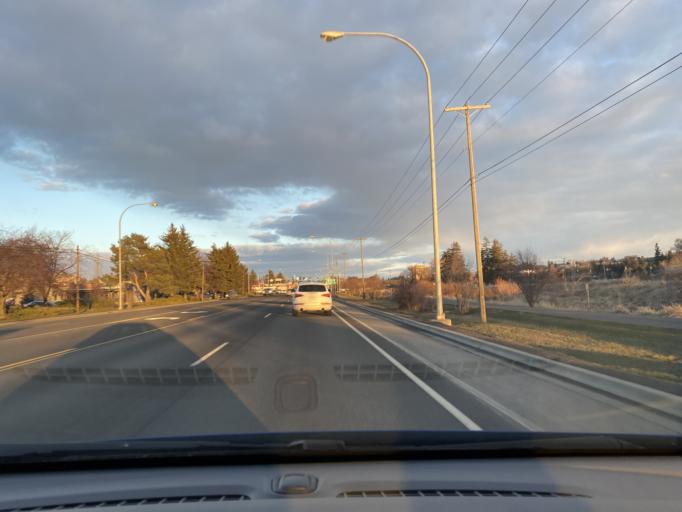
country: US
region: Idaho
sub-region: Latah County
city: Moscow
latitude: 46.7325
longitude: -117.0279
